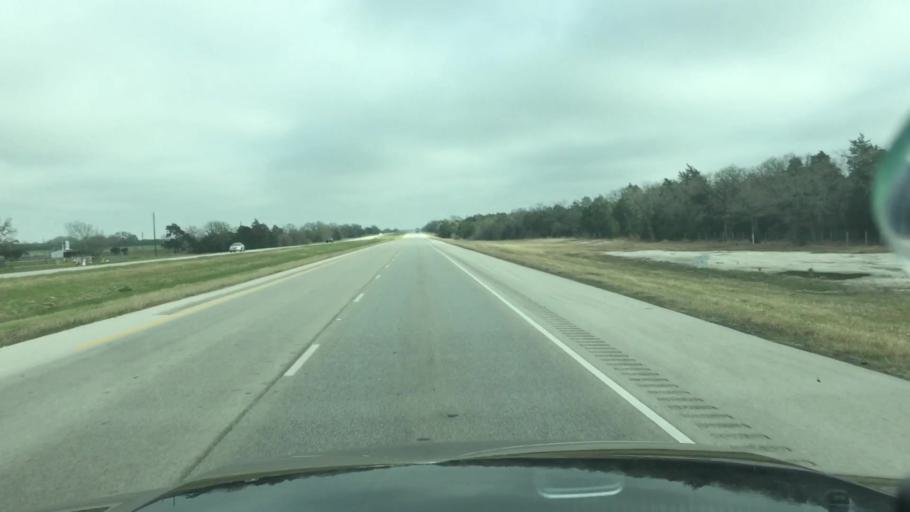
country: US
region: Texas
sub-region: Lee County
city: Giddings
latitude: 30.1437
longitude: -96.7357
